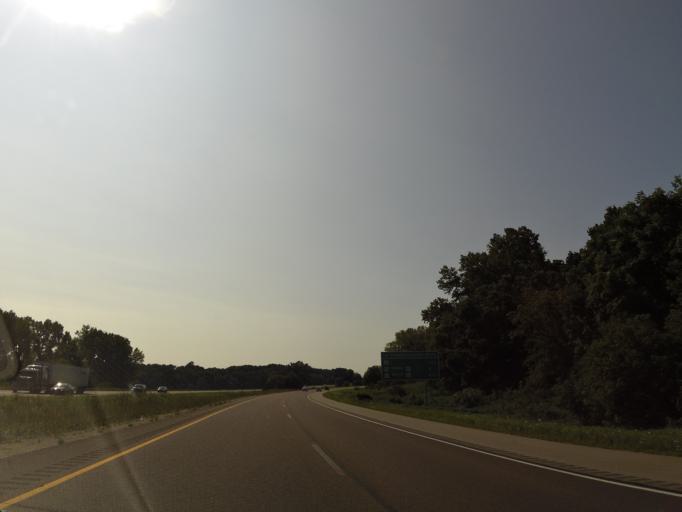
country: US
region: Wisconsin
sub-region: La Crosse County
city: West Salem
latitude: 43.8708
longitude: -91.1467
